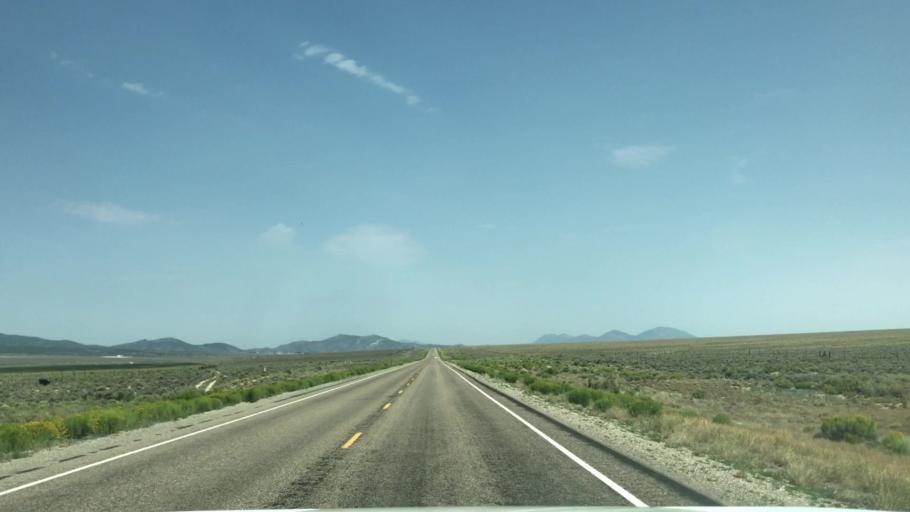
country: US
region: Nevada
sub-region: White Pine County
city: Ely
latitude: 39.1359
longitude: -114.7855
